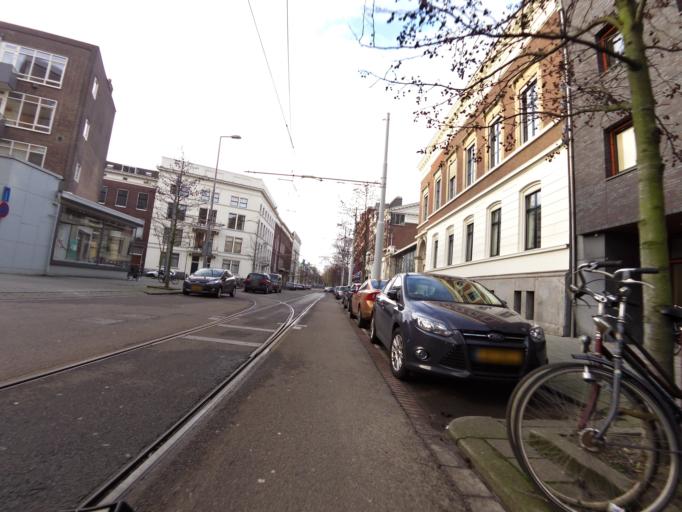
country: NL
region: South Holland
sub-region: Gemeente Rotterdam
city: Rotterdam
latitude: 51.9094
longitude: 4.4808
